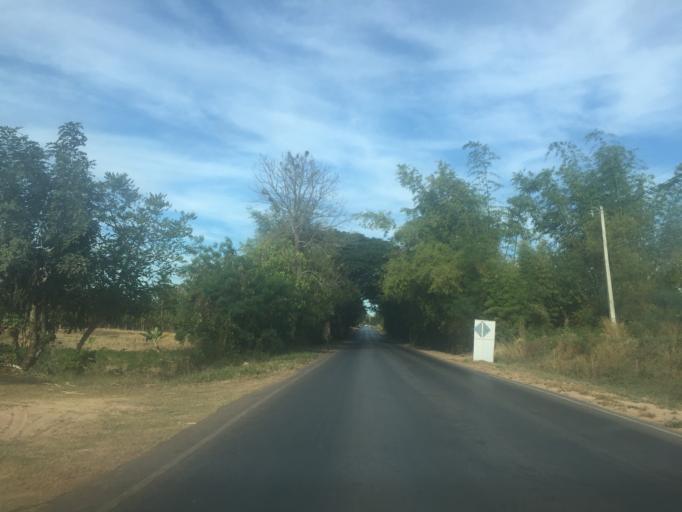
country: TH
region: Changwat Udon Thani
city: Si That
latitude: 16.9772
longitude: 103.1943
